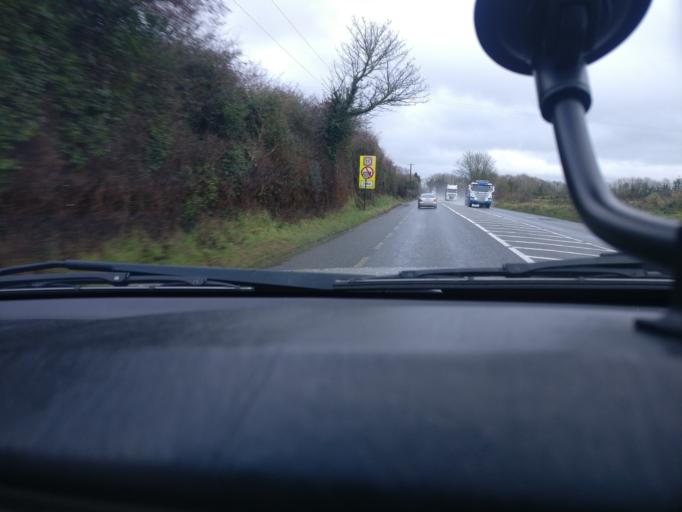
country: IE
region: Leinster
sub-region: An Mhi
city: Enfield
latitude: 53.4191
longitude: -6.7707
